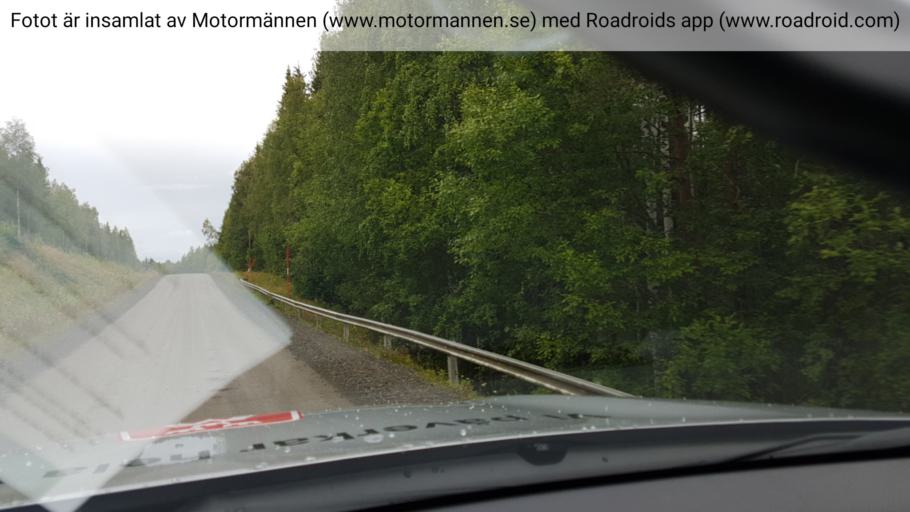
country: SE
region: Norrbotten
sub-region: Alvsbyns Kommun
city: AElvsbyn
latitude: 65.9942
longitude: 21.1848
